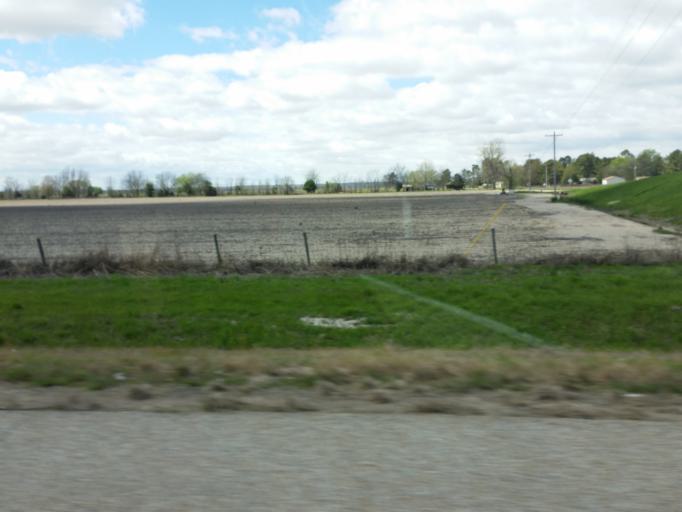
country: US
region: Arkansas
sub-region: Craighead County
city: Bay
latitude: 35.7410
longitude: -90.5802
